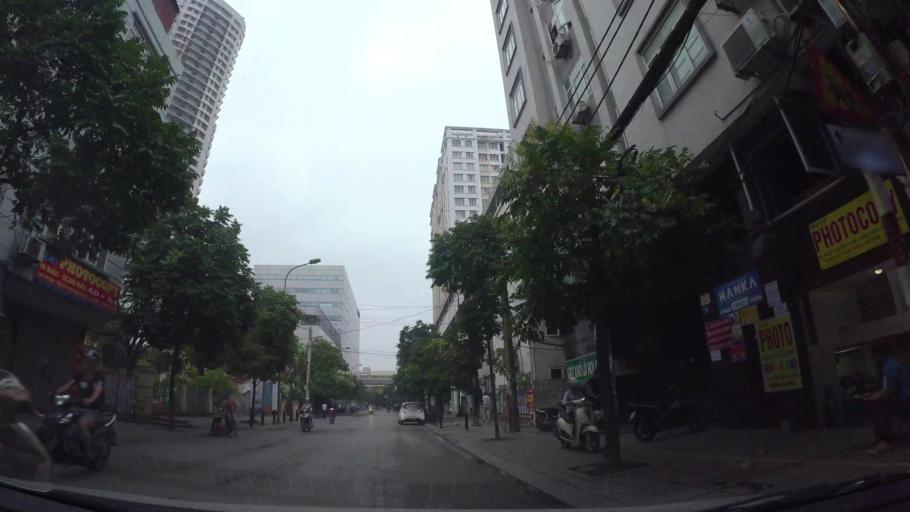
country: VN
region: Ha Noi
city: Cau Giay
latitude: 21.0347
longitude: 105.7836
